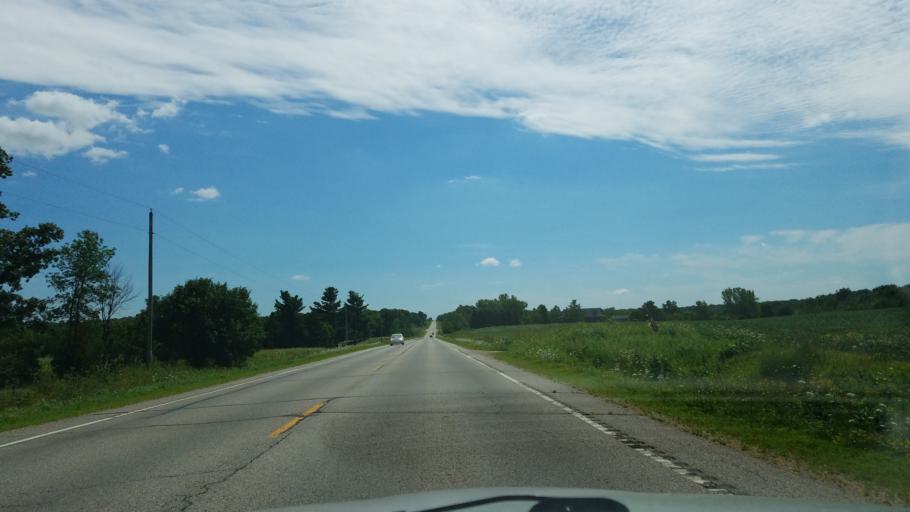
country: US
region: Wisconsin
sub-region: Saint Croix County
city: Glenwood City
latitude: 44.9960
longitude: -92.1966
